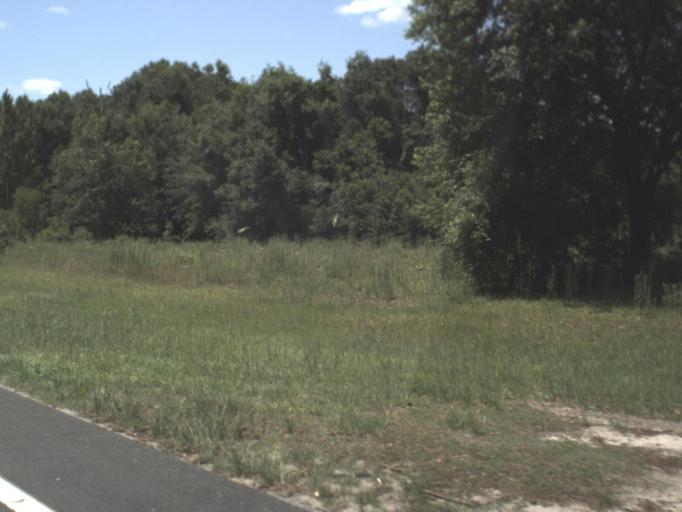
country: US
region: Florida
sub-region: Lafayette County
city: Mayo
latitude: 30.1034
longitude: -83.2440
